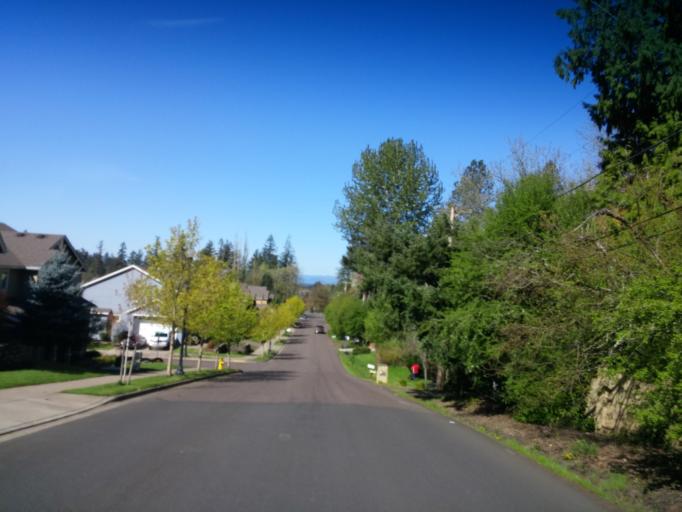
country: US
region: Oregon
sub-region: Washington County
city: West Haven
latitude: 45.5160
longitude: -122.7768
